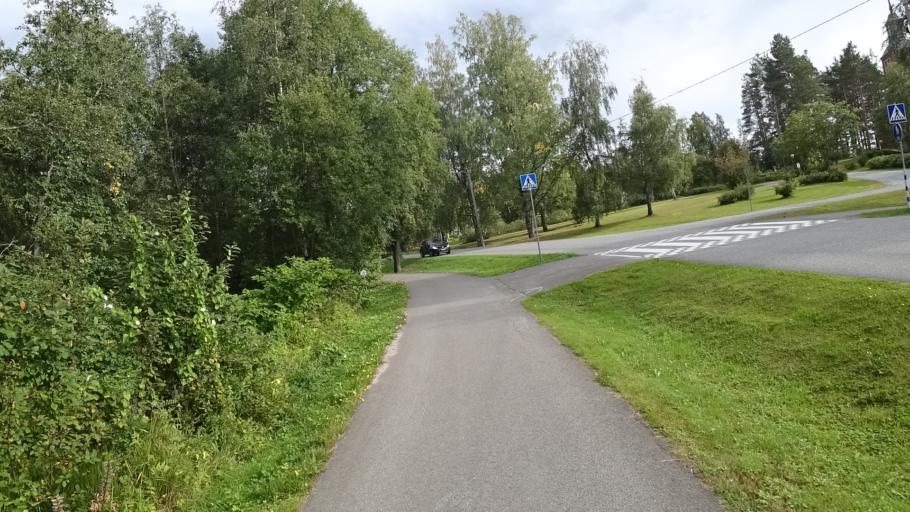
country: FI
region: North Karelia
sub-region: Joensuu
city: Ilomantsi
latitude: 62.6765
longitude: 30.9163
